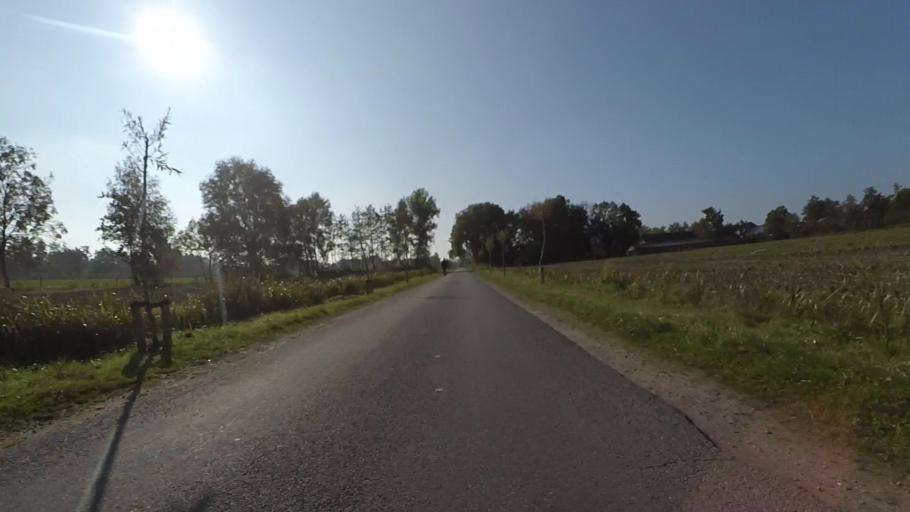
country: NL
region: Gelderland
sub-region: Gemeente Barneveld
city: Zwartebroek
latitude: 52.1930
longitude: 5.4809
